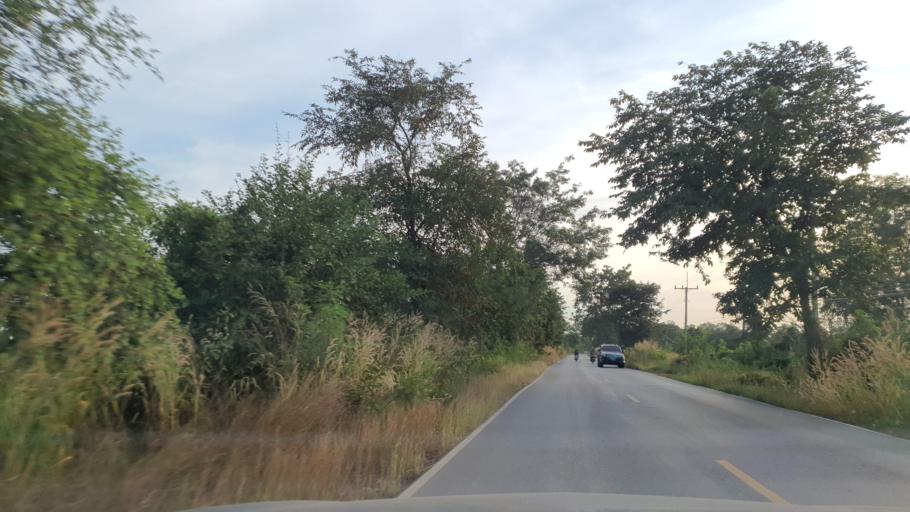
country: TH
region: Nakhon Sawan
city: Nakhon Sawan
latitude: 15.6622
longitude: 100.0518
